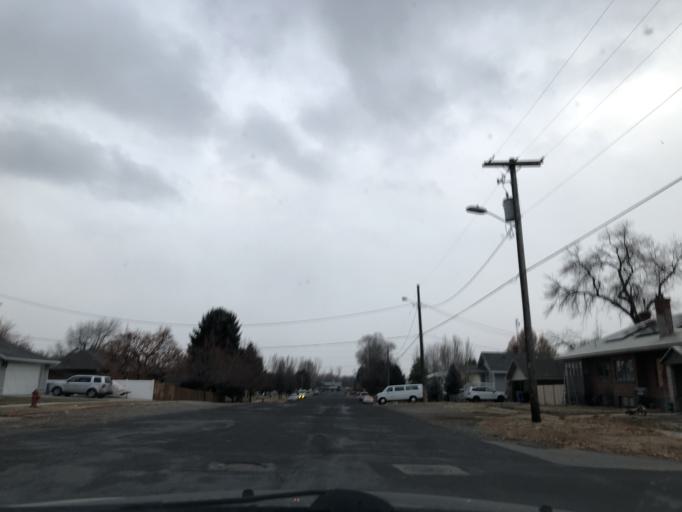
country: US
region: Utah
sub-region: Cache County
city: Logan
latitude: 41.7279
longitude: -111.8480
